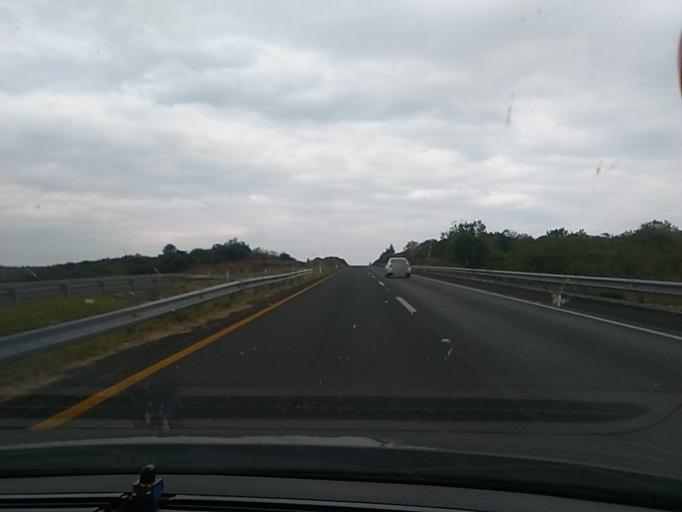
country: MX
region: Michoacan
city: Penjamillo de Degollado
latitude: 20.0022
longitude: -101.8886
